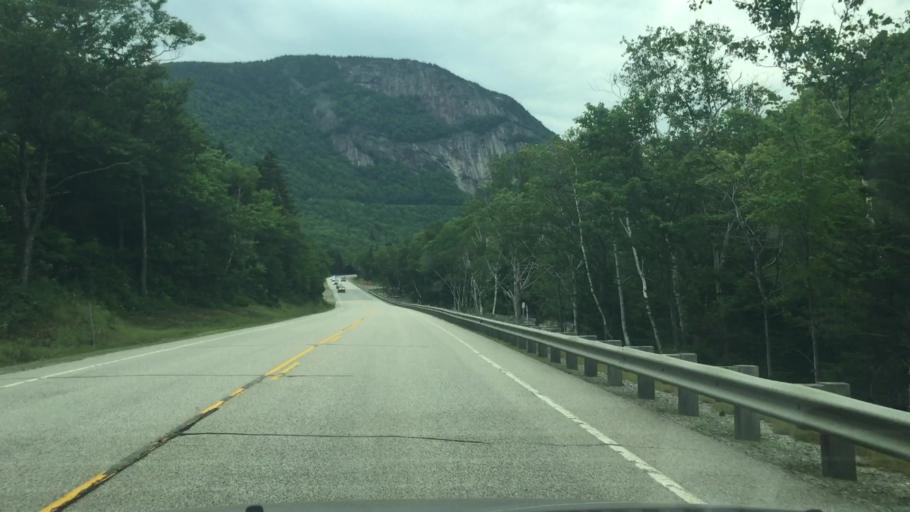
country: US
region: New Hampshire
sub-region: Grafton County
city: Deerfield
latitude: 44.1884
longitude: -71.4029
